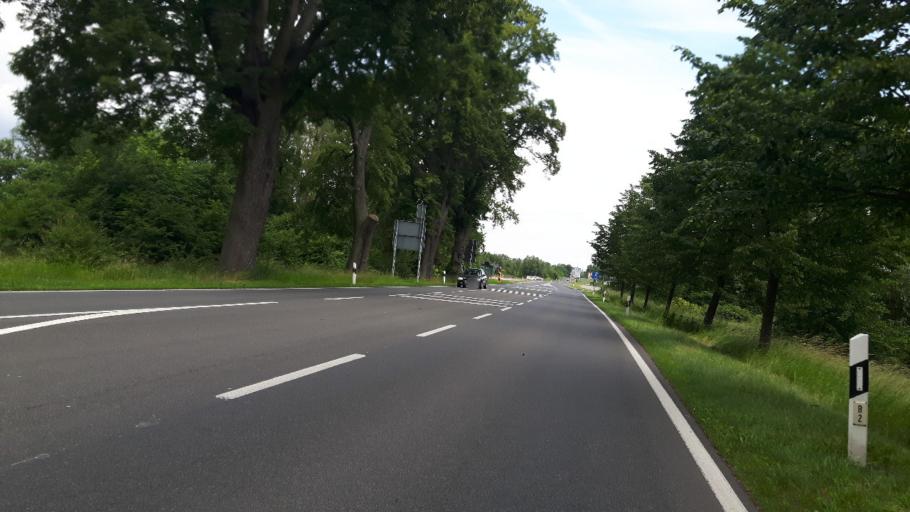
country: PL
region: West Pomeranian Voivodeship
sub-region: Powiat policki
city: Kolbaskowo
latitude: 53.3060
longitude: 14.4087
